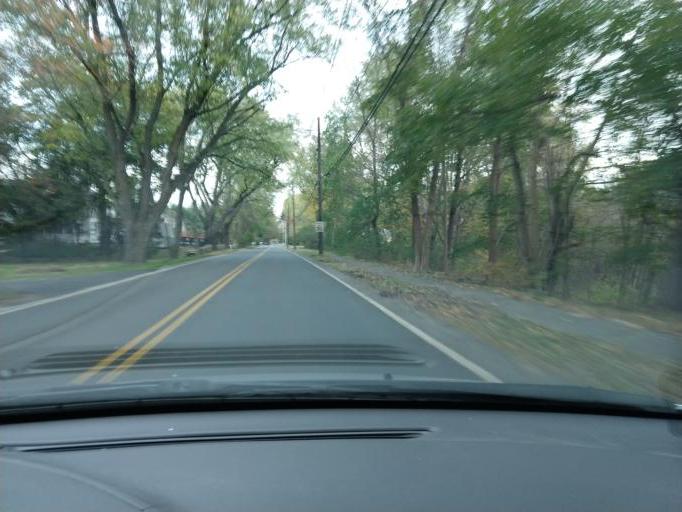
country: US
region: Massachusetts
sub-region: Middlesex County
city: West Concord
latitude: 42.4727
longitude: -71.3866
